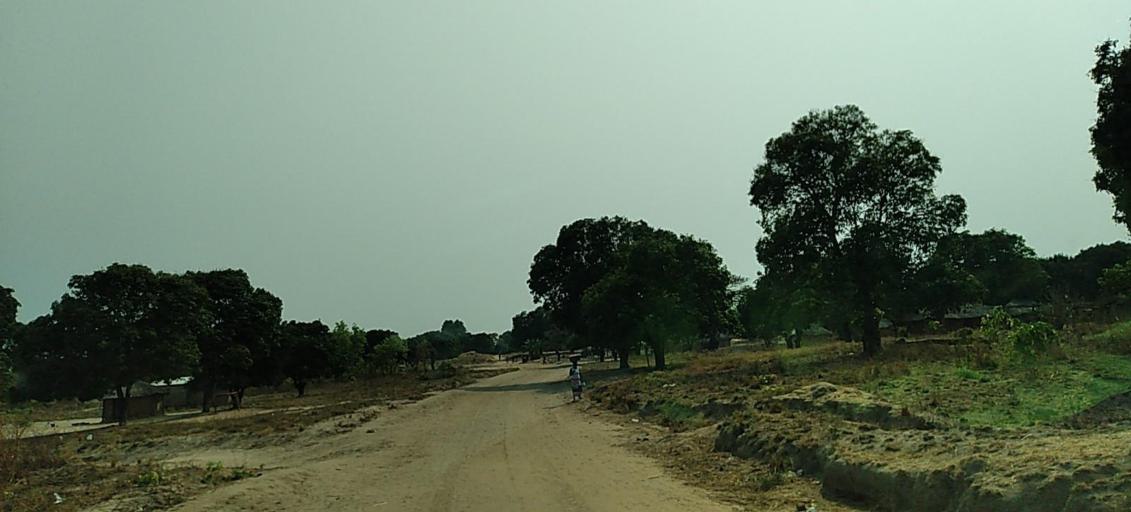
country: ZM
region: North-Western
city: Zambezi
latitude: -13.1700
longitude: 23.4046
